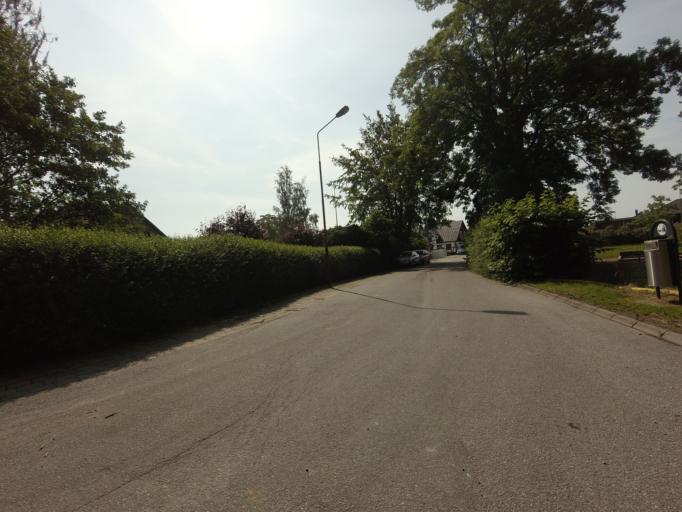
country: SE
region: Skane
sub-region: Malmo
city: Tygelsjo
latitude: 55.5174
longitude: 13.0052
